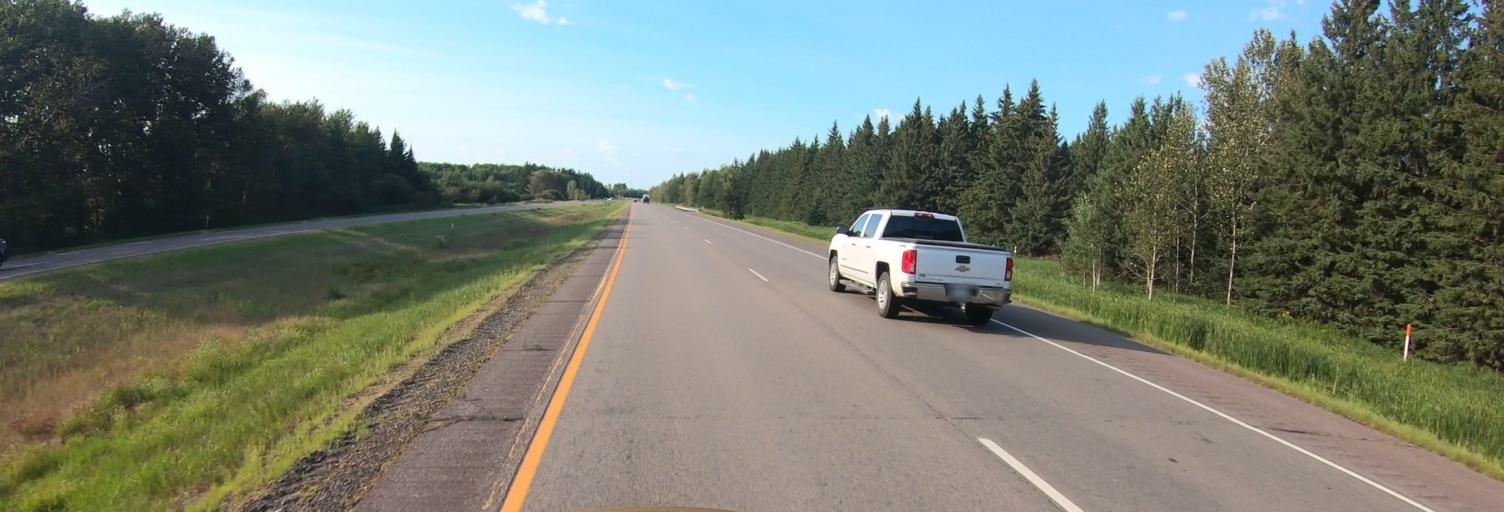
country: US
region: Minnesota
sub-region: Saint Louis County
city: Eveleth
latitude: 47.1310
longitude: -92.4722
